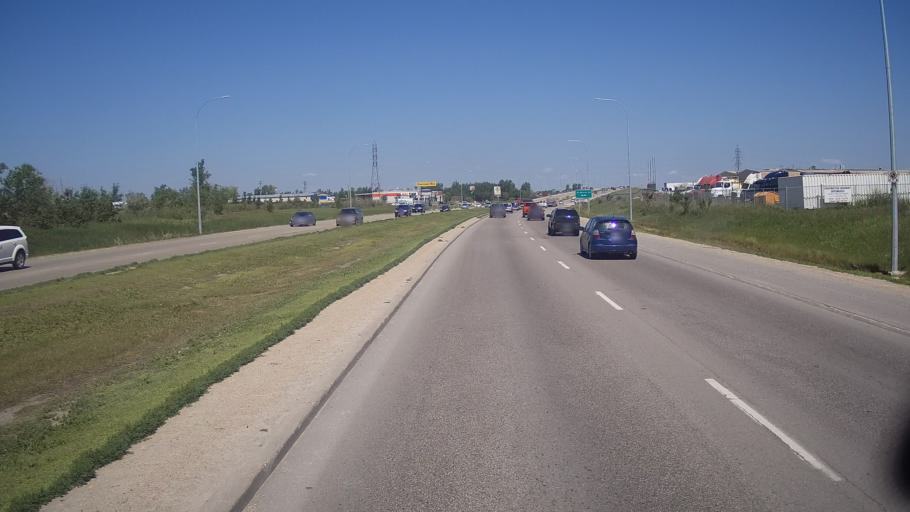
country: CA
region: Manitoba
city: Winnipeg
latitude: 49.8879
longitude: -97.0722
